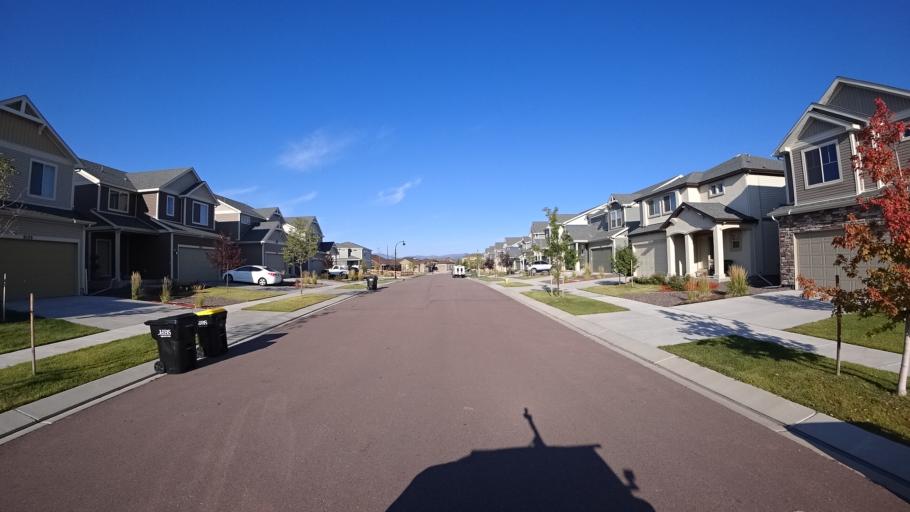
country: US
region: Colorado
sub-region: El Paso County
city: Cimarron Hills
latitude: 38.9358
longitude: -104.6574
